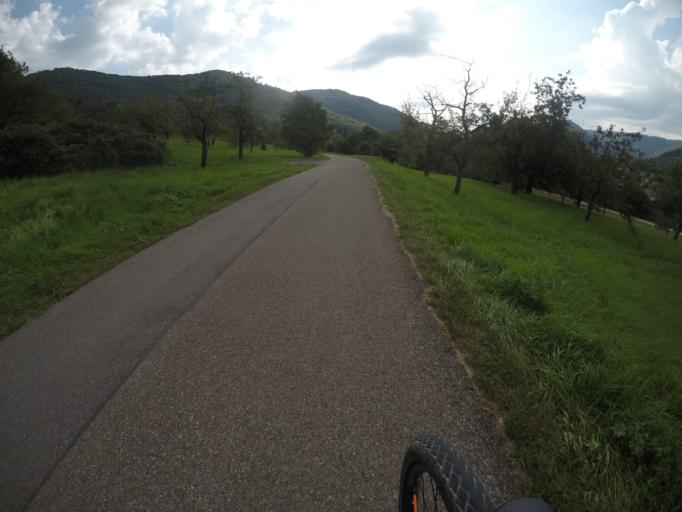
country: DE
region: Baden-Wuerttemberg
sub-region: Tuebingen Region
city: Dettingen an der Erms
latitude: 48.5145
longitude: 9.3670
